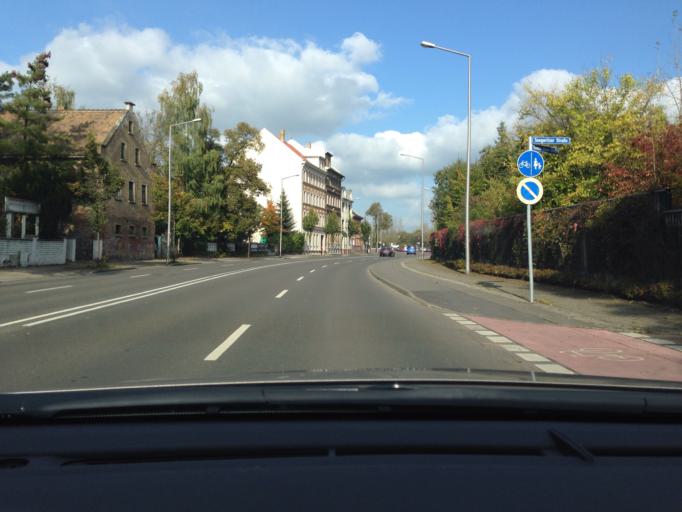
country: DE
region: Saxony
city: Taucha
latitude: 51.3479
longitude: 12.4459
